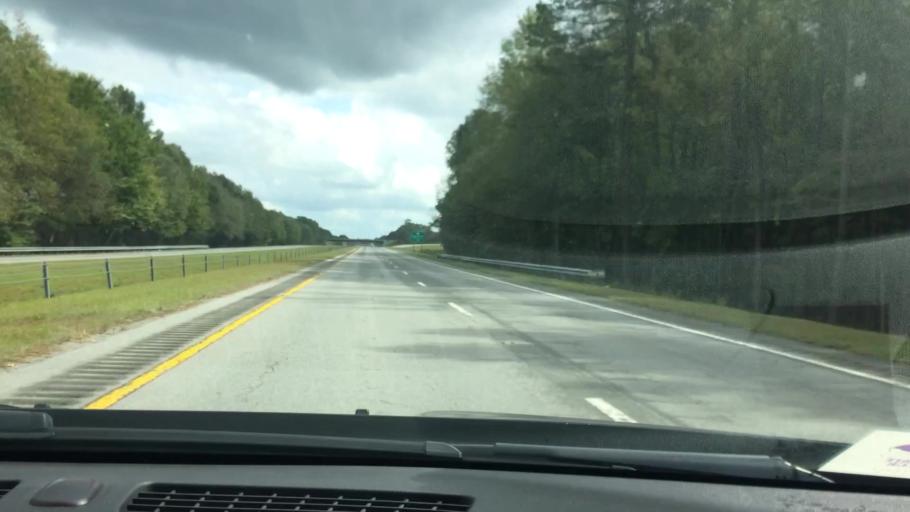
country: US
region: North Carolina
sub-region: Pitt County
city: Farmville
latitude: 35.6184
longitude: -77.6859
